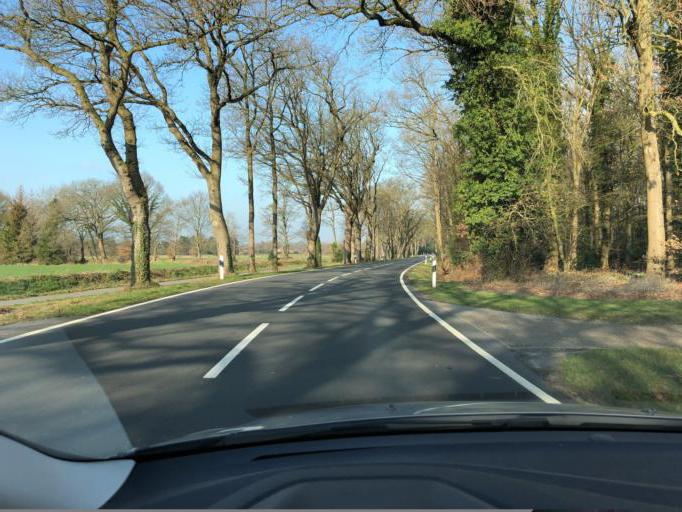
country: DE
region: Lower Saxony
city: Westerstede
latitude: 53.2661
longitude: 7.9105
